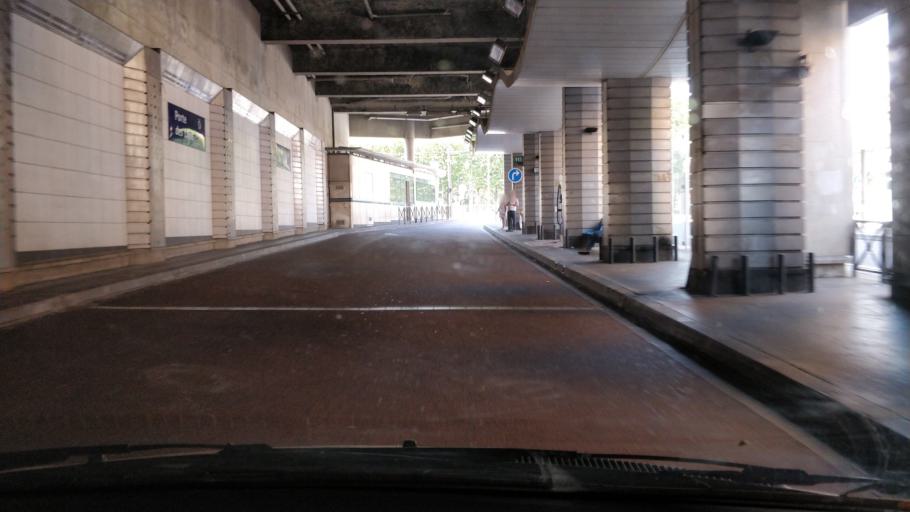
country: FR
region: Ile-de-France
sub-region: Departement de Seine-Saint-Denis
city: Le Pre-Saint-Gervais
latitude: 48.8766
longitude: 2.4083
